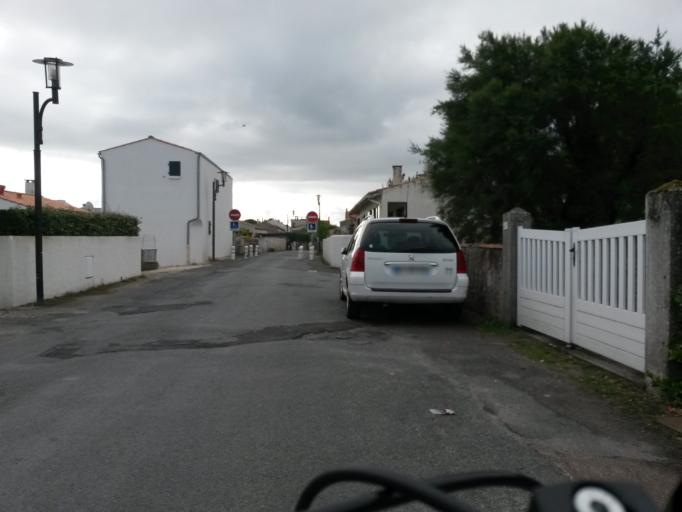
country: FR
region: Poitou-Charentes
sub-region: Departement de la Charente-Maritime
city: Dolus-d'Oleron
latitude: 45.9195
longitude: -1.3365
